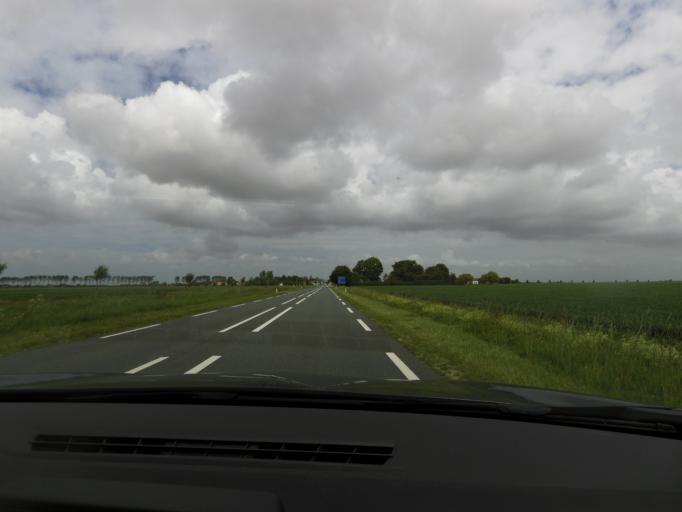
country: NL
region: Zeeland
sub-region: Schouwen-Duiveland
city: Scharendijke
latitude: 51.7035
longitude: 3.9457
